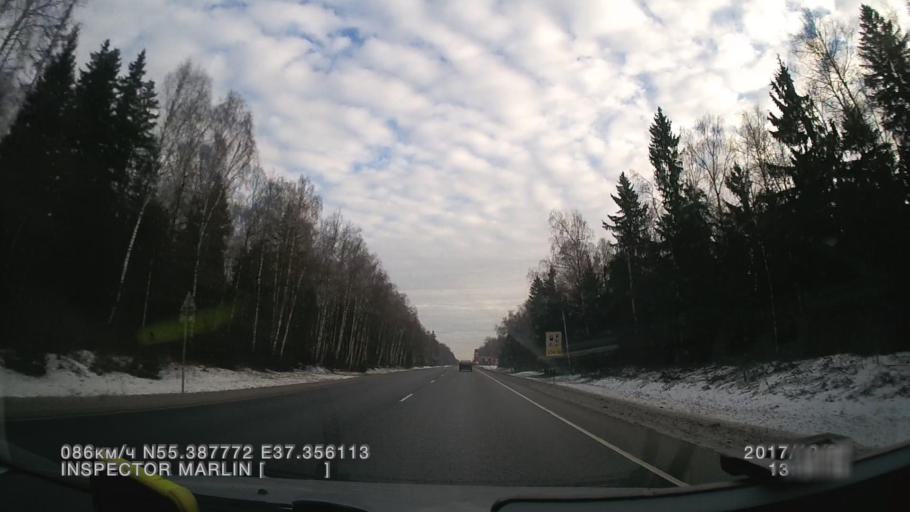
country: RU
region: Moskovskaya
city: Troitsk
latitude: 55.3877
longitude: 37.3564
